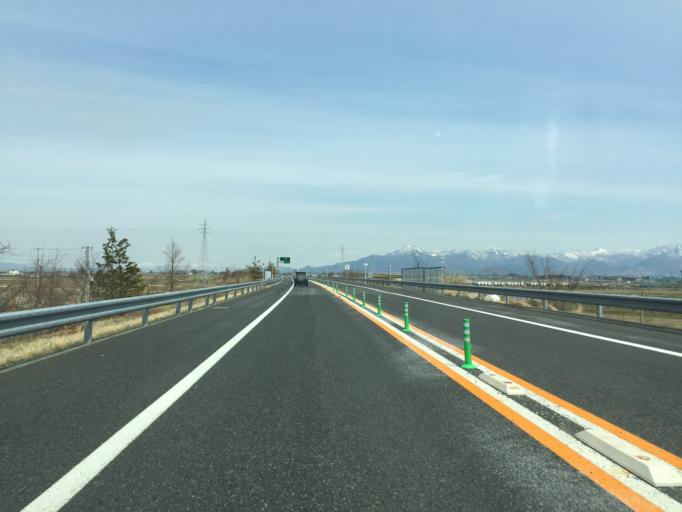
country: JP
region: Yamagata
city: Tendo
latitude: 38.3581
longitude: 140.3437
